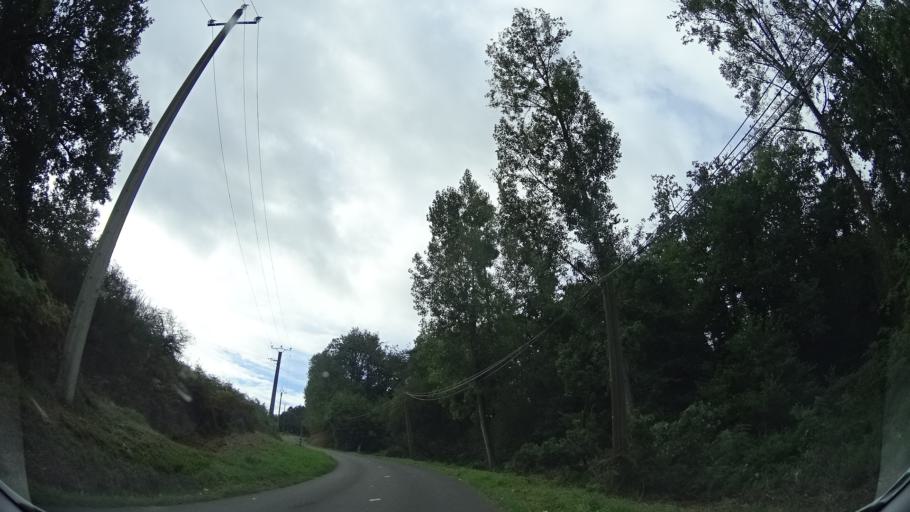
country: FR
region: Brittany
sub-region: Departement d'Ille-et-Vilaine
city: Tinteniac
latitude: 48.2889
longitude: -1.8530
